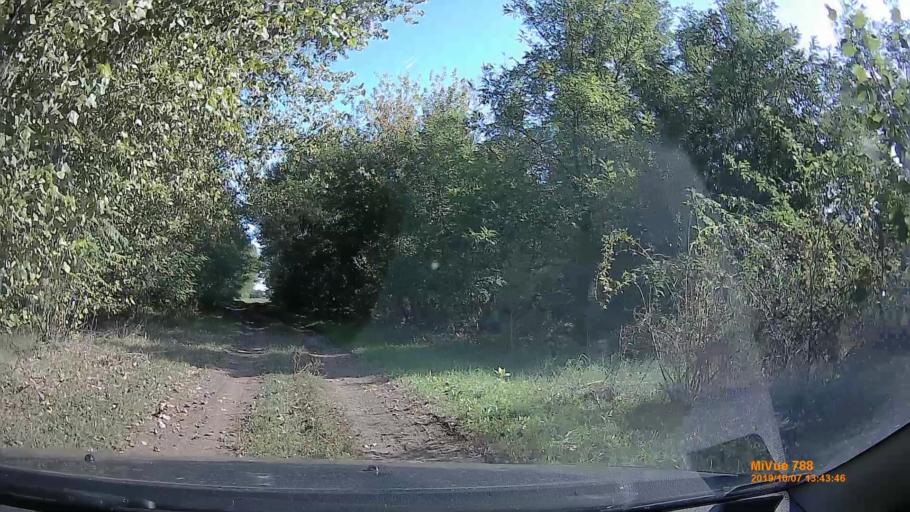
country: HU
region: Jasz-Nagykun-Szolnok
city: Cserkeszolo
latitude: 46.8811
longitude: 20.1985
